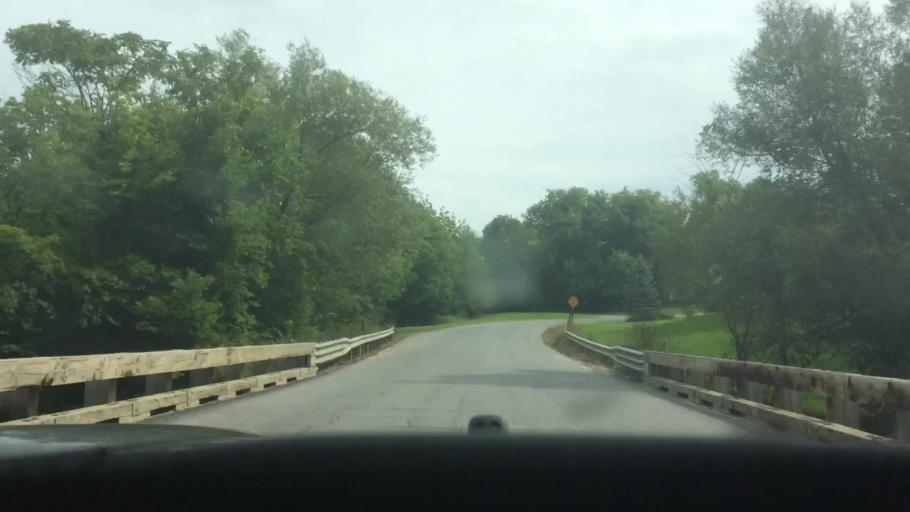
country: US
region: New York
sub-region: St. Lawrence County
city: Canton
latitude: 44.4699
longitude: -75.2333
